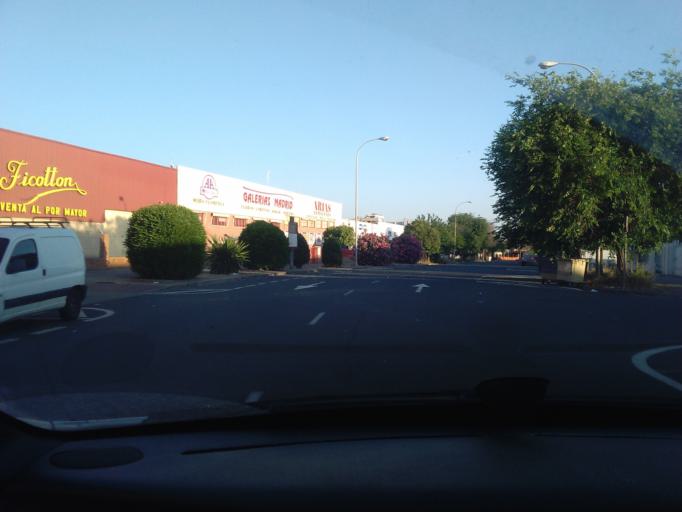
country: ES
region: Andalusia
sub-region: Provincia de Sevilla
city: Sevilla
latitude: 37.3953
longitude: -5.9392
